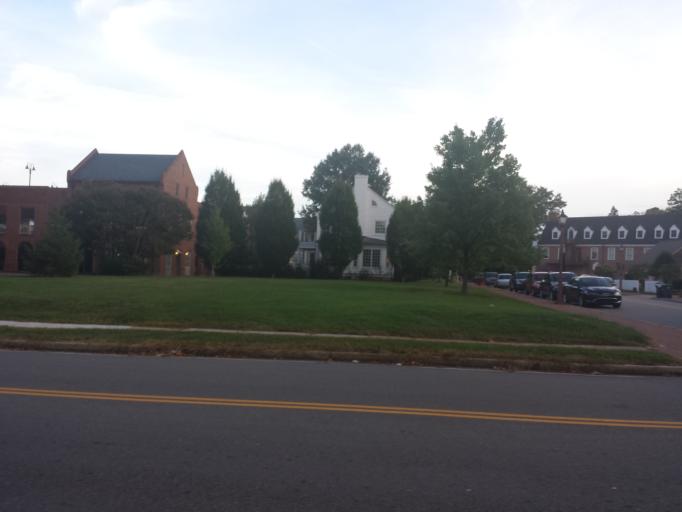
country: US
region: Virginia
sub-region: City of Williamsburg
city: Williamsburg
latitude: 37.2735
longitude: -76.7075
